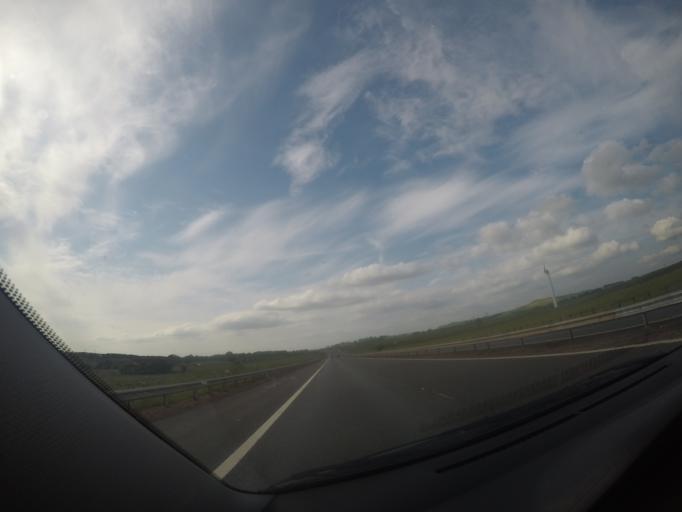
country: GB
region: Scotland
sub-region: South Lanarkshire
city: Lesmahagow
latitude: 55.6174
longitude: -3.8515
